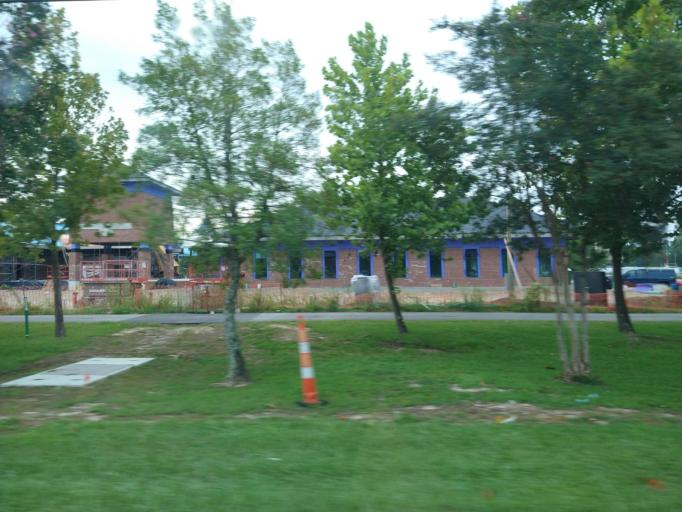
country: US
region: North Carolina
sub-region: Onslow County
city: Jacksonville
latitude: 34.7657
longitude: -77.4086
